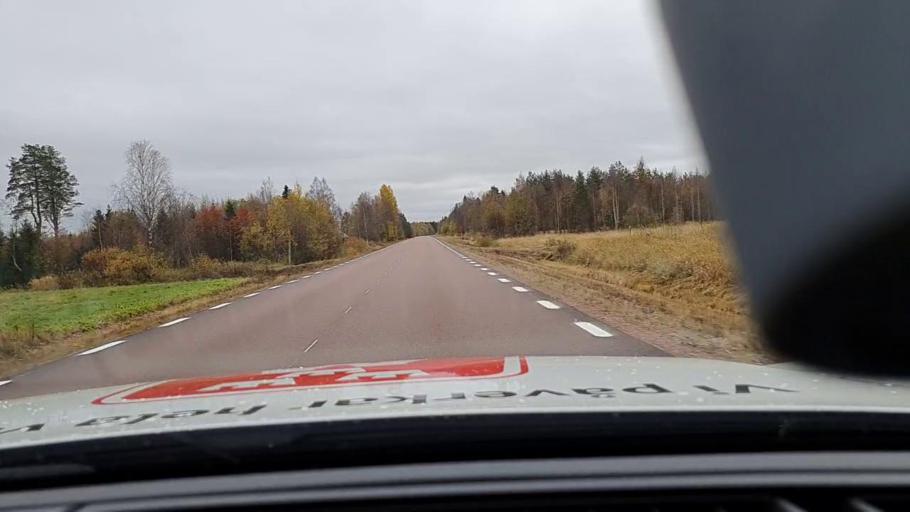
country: FI
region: Lapland
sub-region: Kemi-Tornio
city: Tornio
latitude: 66.0561
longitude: 23.9335
